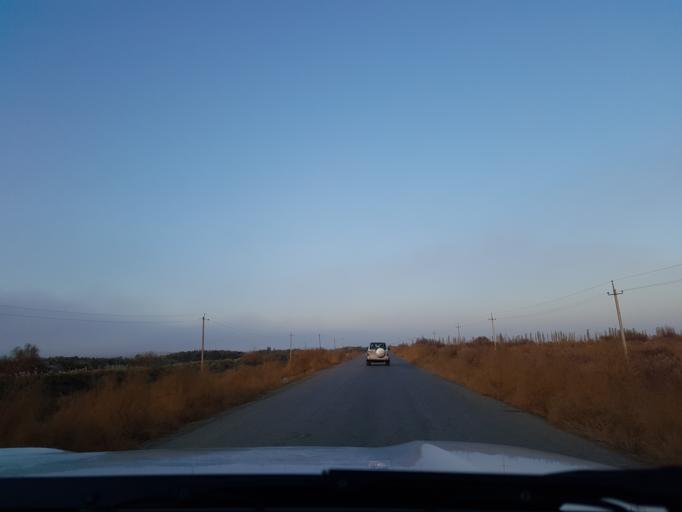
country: TM
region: Dasoguz
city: Koeneuergench
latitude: 41.8440
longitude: 58.6525
